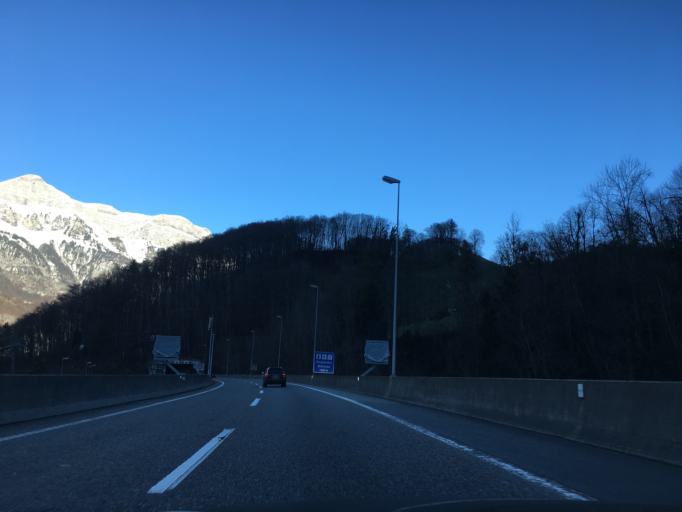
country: CH
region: Saint Gallen
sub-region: Wahlkreis Sarganserland
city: Quarten
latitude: 47.1070
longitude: 9.2479
